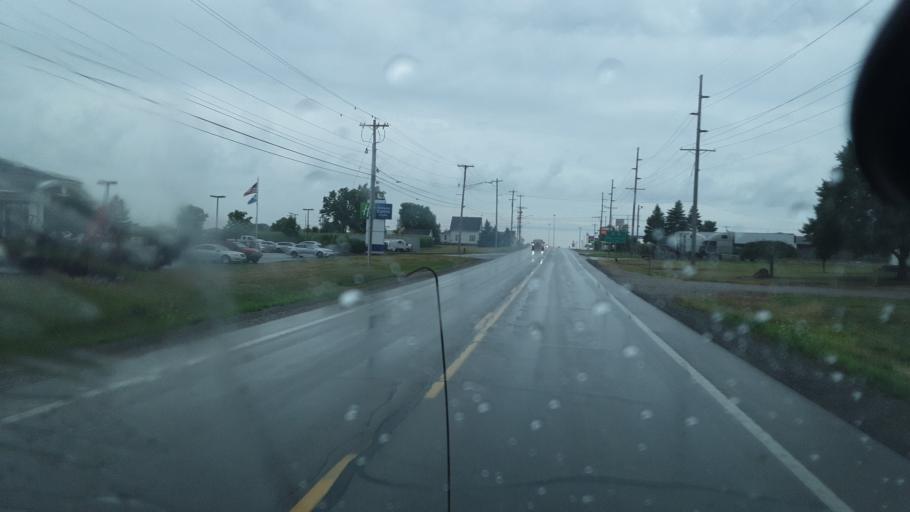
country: US
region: Ohio
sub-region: Williams County
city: Montpelier
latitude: 41.6061
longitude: -84.5556
